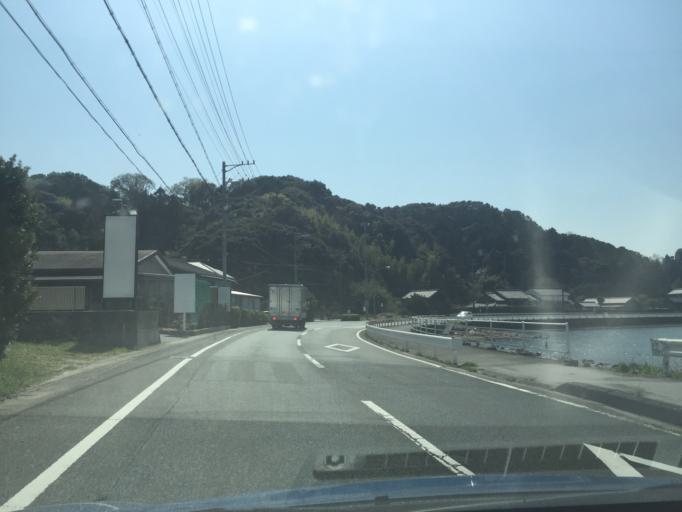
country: JP
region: Shizuoka
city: Hamamatsu
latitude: 34.7839
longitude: 137.6426
